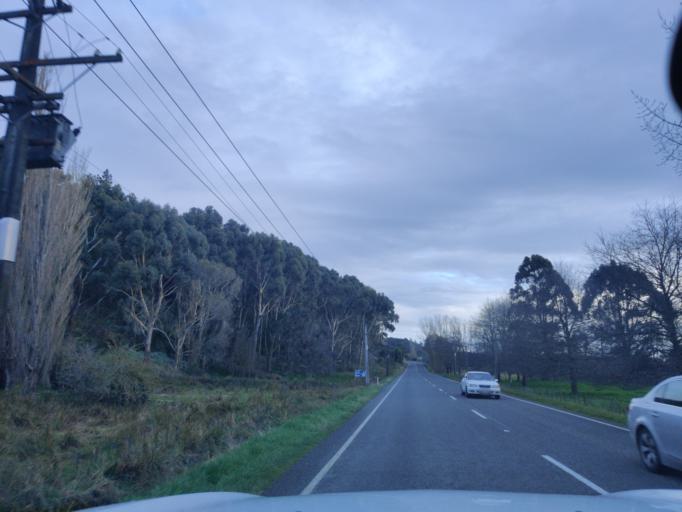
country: NZ
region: Manawatu-Wanganui
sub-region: Palmerston North City
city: Palmerston North
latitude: -40.3704
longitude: 175.6559
